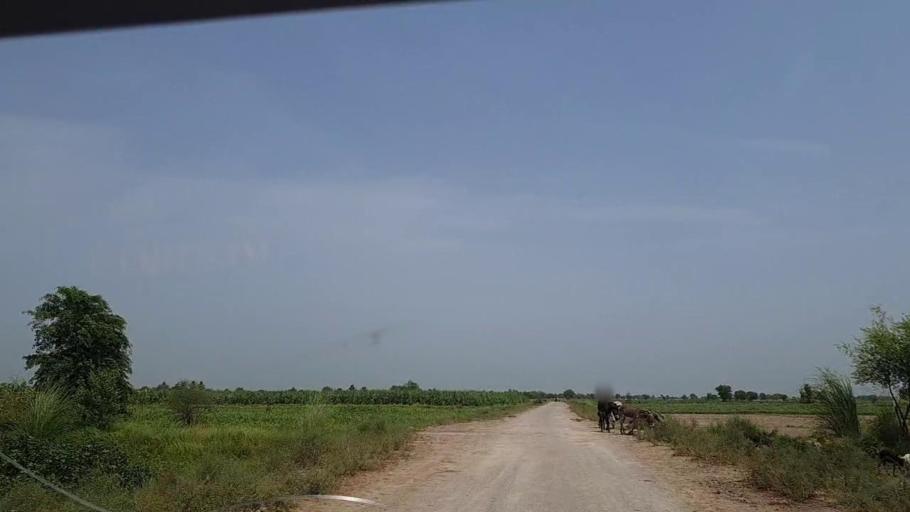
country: PK
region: Sindh
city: Tharu Shah
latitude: 26.9084
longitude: 68.0531
